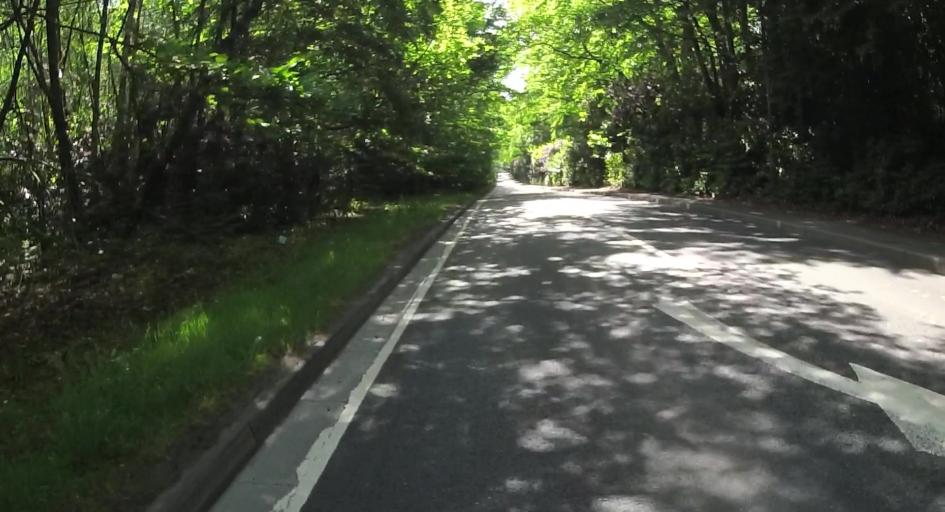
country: GB
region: England
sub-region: Bracknell Forest
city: Crowthorne
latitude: 51.3827
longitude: -0.8085
